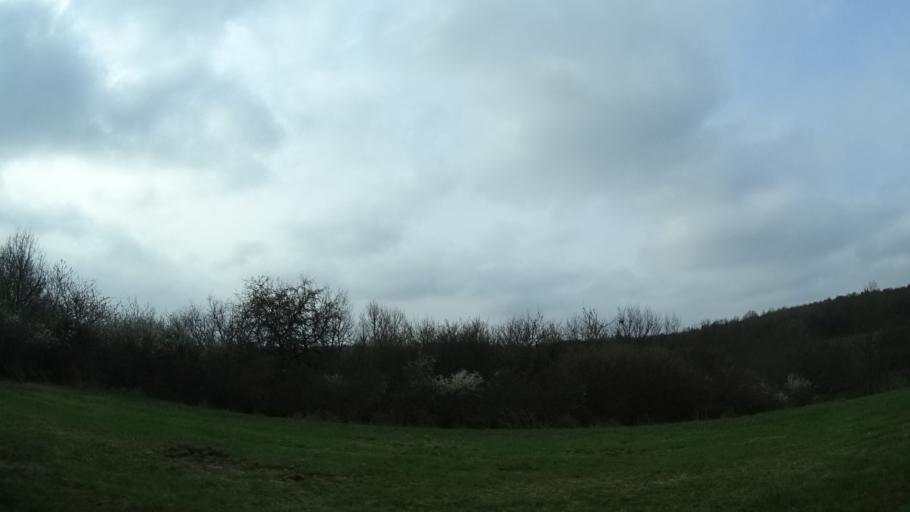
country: DE
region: Rheinland-Pfalz
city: Siesbach
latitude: 49.7304
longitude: 7.2302
